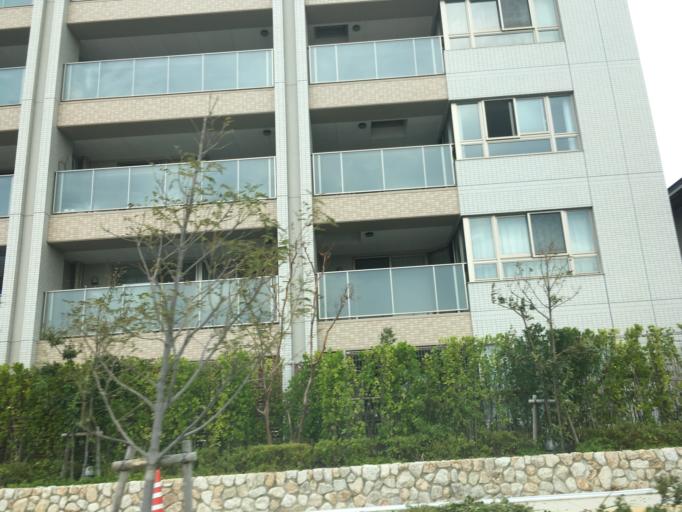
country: JP
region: Hyogo
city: Nishinomiya-hama
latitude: 34.7076
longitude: 135.3209
